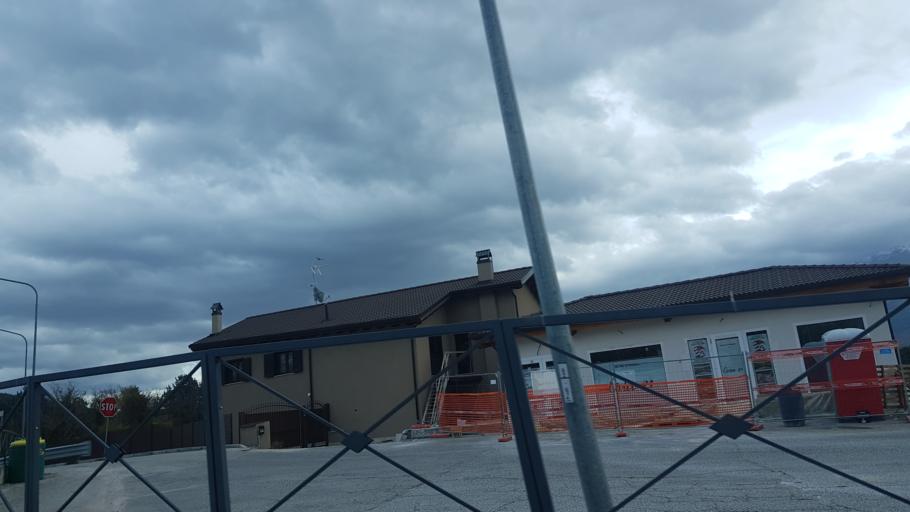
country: IT
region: Abruzzo
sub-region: Provincia dell' Aquila
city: L'Aquila
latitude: 42.3519
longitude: 13.4187
